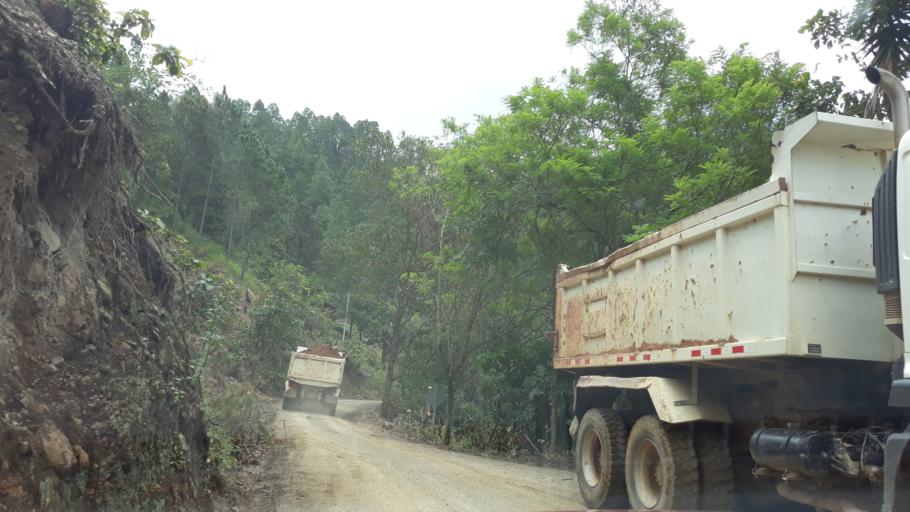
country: HN
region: El Paraiso
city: Santa Cruz
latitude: 13.7553
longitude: -86.6542
